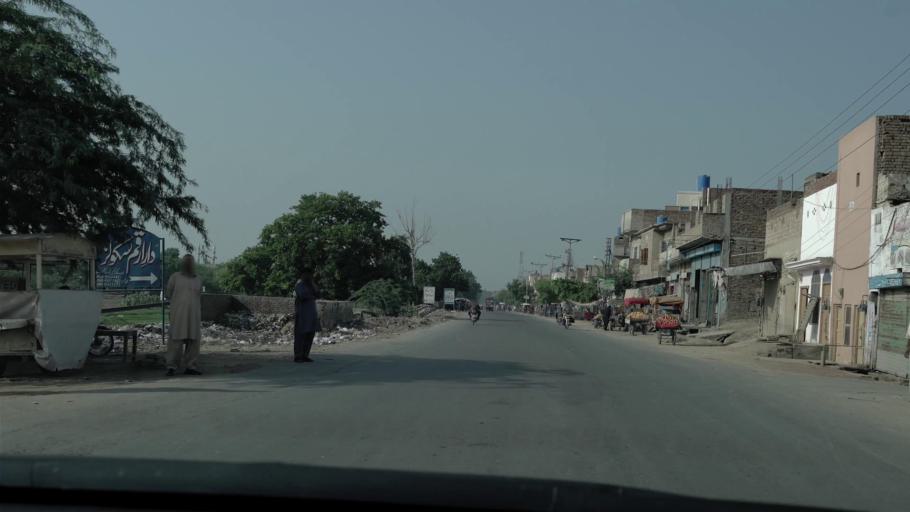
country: PK
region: Punjab
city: Gojra
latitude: 31.1254
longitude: 72.6719
